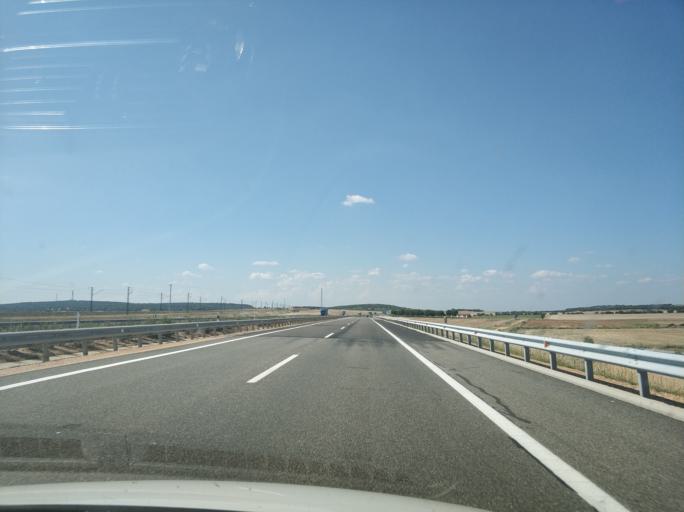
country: ES
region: Castille and Leon
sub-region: Provincia de Zamora
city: Montamarta
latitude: 41.6685
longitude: -5.8010
